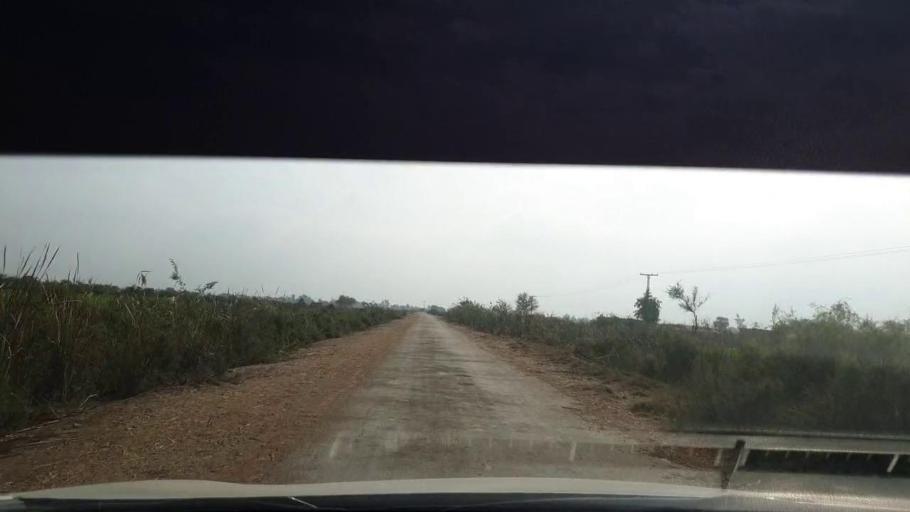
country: PK
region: Sindh
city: Berani
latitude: 25.7669
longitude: 68.8762
